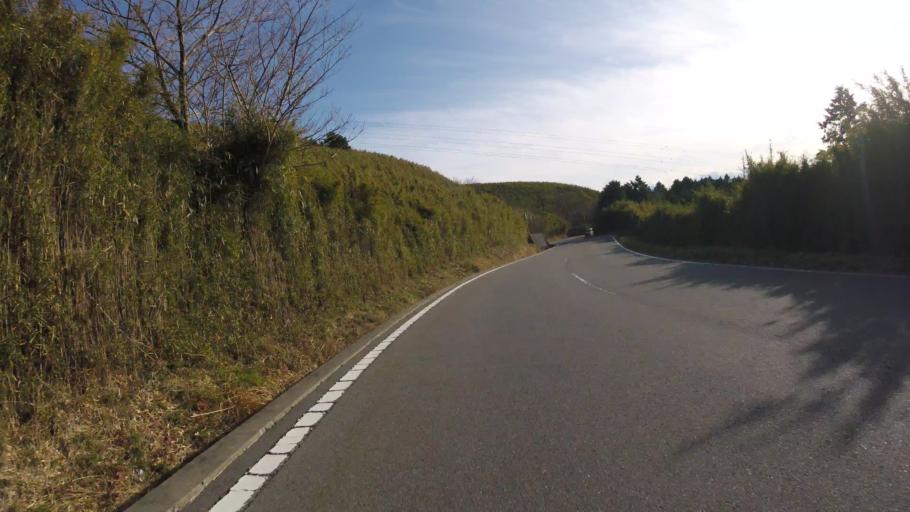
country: JP
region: Kanagawa
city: Yugawara
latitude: 35.1352
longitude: 139.0374
